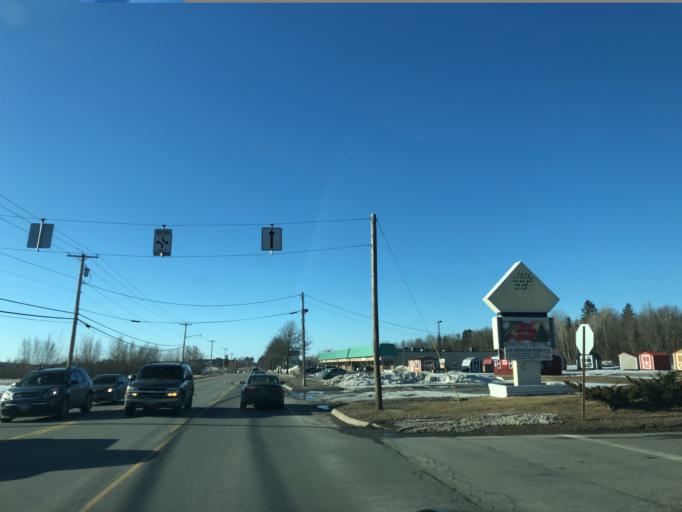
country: US
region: Maine
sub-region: Penobscot County
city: Bangor
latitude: 44.8371
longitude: -68.7924
